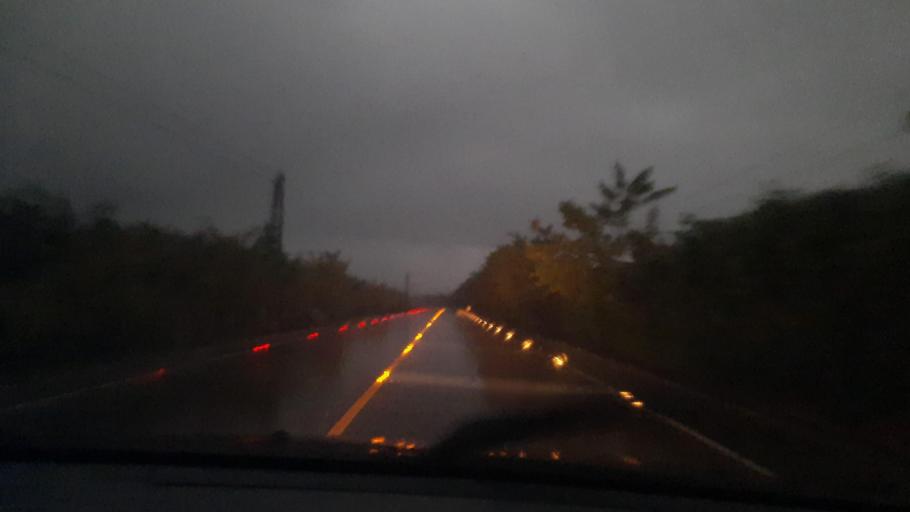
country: HN
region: Cortes
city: Potrerillos
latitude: 15.6413
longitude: -88.4218
